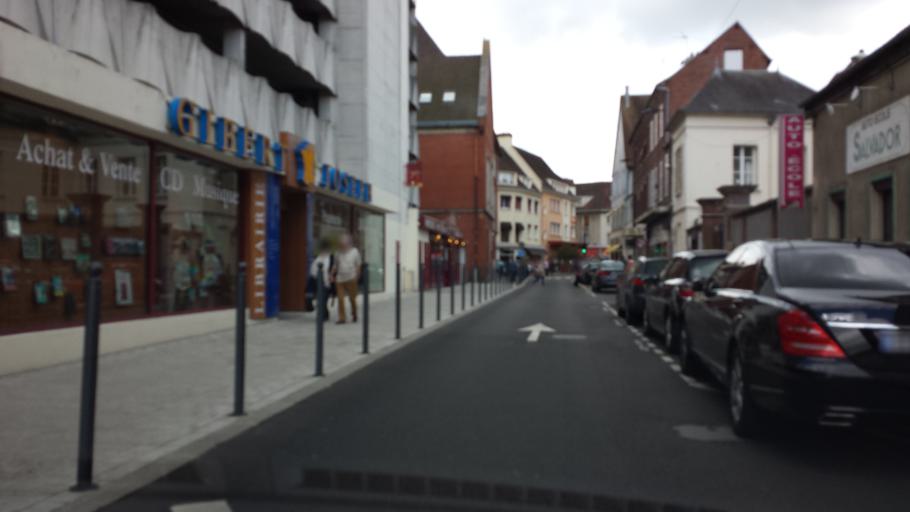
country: FR
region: Haute-Normandie
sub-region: Departement de l'Eure
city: Evreux
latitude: 49.0273
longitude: 1.1473
